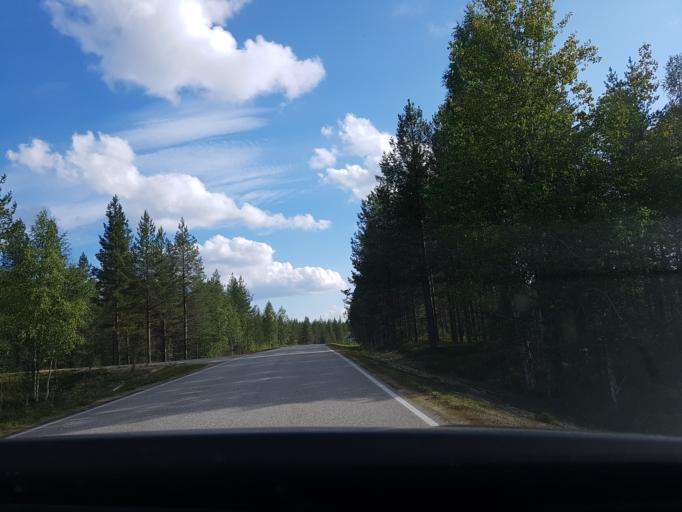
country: FI
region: Kainuu
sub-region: Kehys-Kainuu
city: Kuhmo
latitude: 64.6234
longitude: 29.6978
